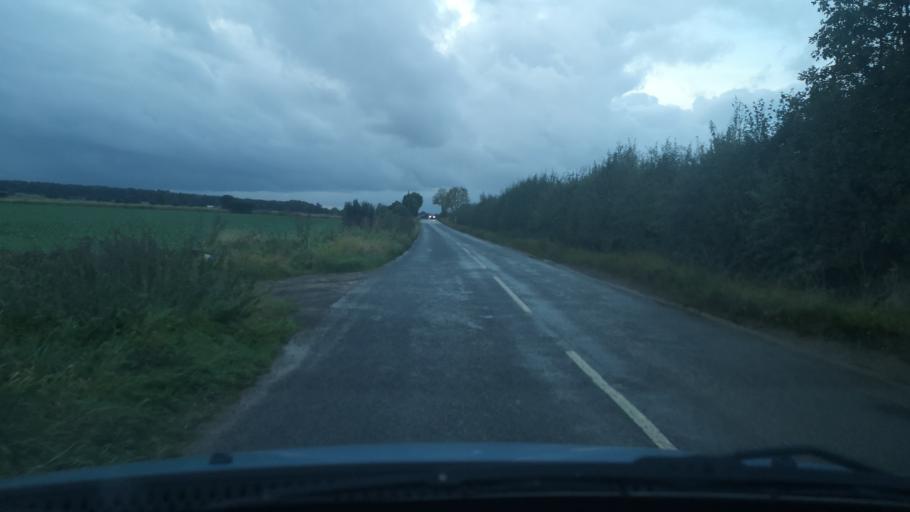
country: GB
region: England
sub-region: City and Borough of Wakefield
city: Darrington
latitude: 53.6462
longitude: -1.2462
